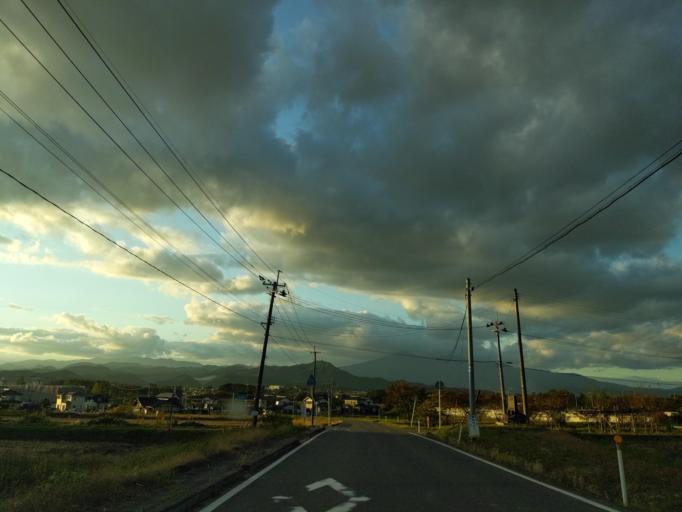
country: JP
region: Fukushima
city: Motomiya
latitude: 37.4795
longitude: 140.4013
